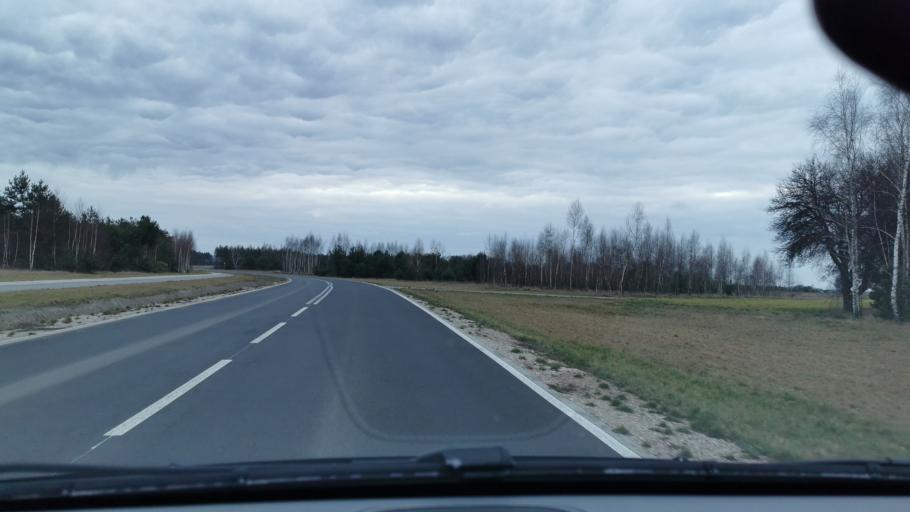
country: PL
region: Masovian Voivodeship
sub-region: Powiat zyrardowski
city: Zyrardow
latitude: 51.9990
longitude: 20.4637
